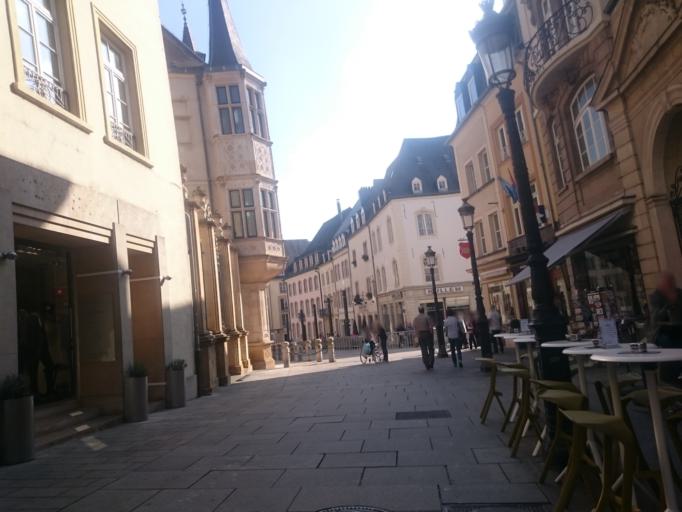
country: LU
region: Luxembourg
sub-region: Canton de Luxembourg
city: Luxembourg
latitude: 49.6112
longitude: 6.1325
